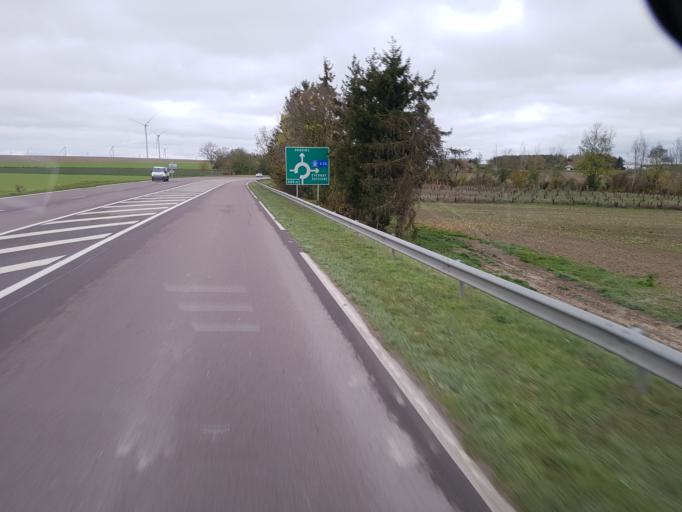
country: FR
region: Champagne-Ardenne
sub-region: Departement de l'Aube
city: Mery-sur-Seine
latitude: 48.4724
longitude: 3.8765
